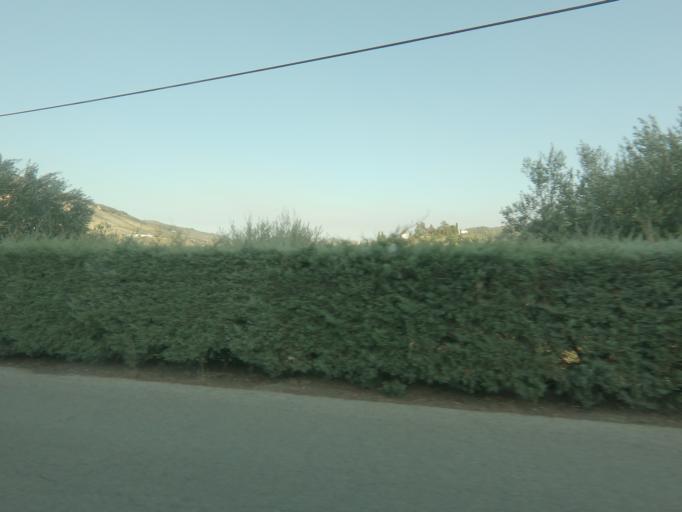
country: PT
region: Vila Real
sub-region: Sabrosa
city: Vilela
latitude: 41.1640
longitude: -7.6320
